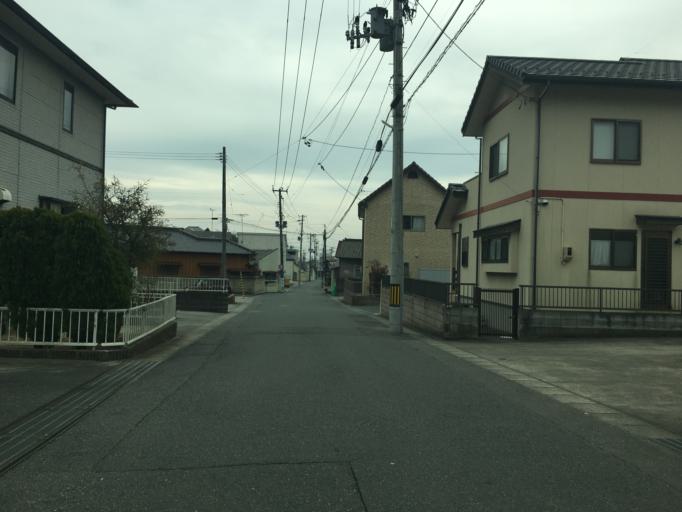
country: JP
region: Fukushima
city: Iwaki
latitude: 36.9527
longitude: 140.9116
